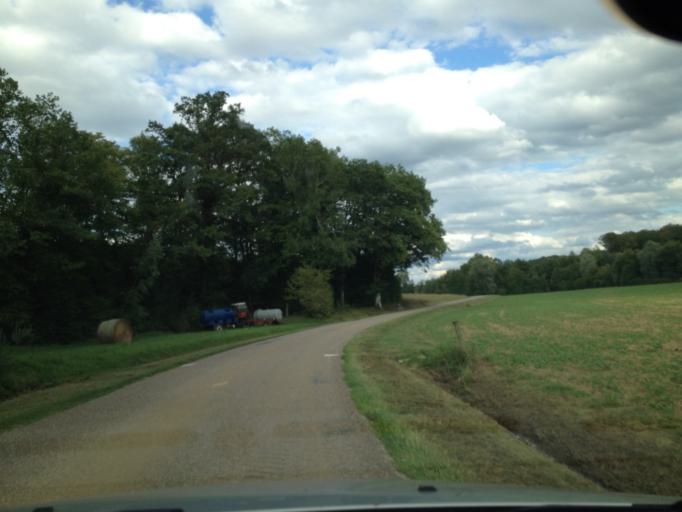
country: FR
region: Franche-Comte
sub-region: Departement de la Haute-Saone
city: Jussey
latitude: 47.8671
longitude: 5.9977
